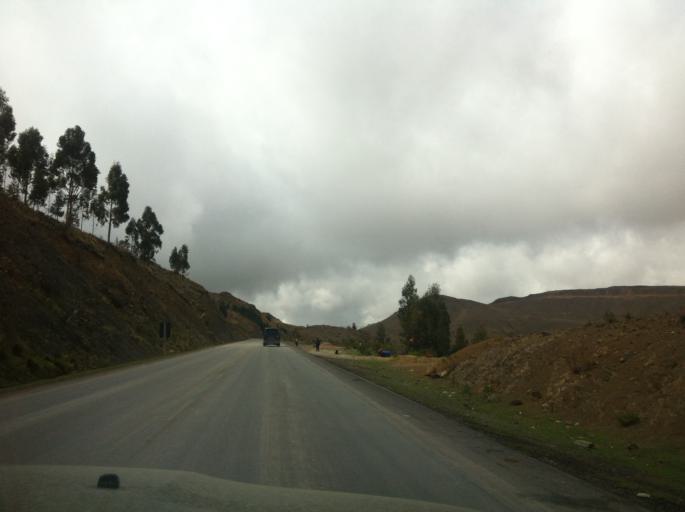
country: BO
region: Cochabamba
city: Irpa Irpa
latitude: -17.6524
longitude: -66.4828
